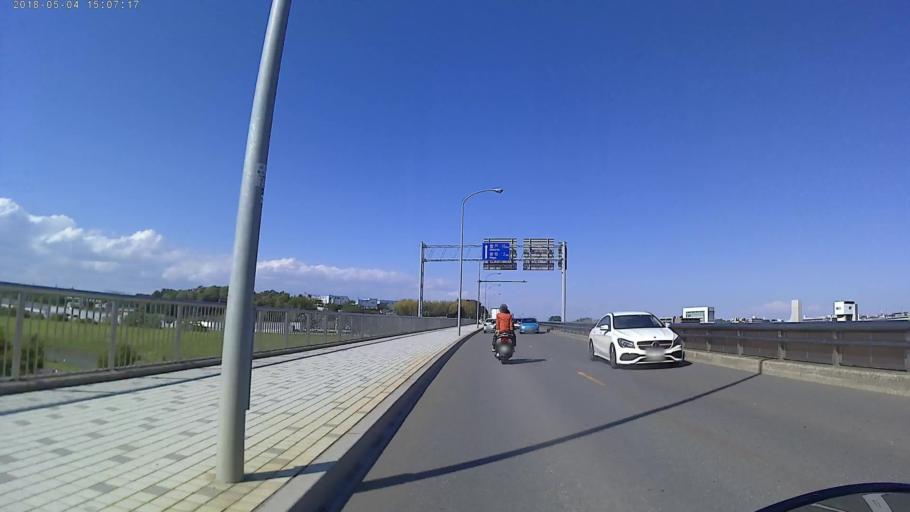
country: JP
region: Kanagawa
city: Yokohama
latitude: 35.5129
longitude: 139.6061
